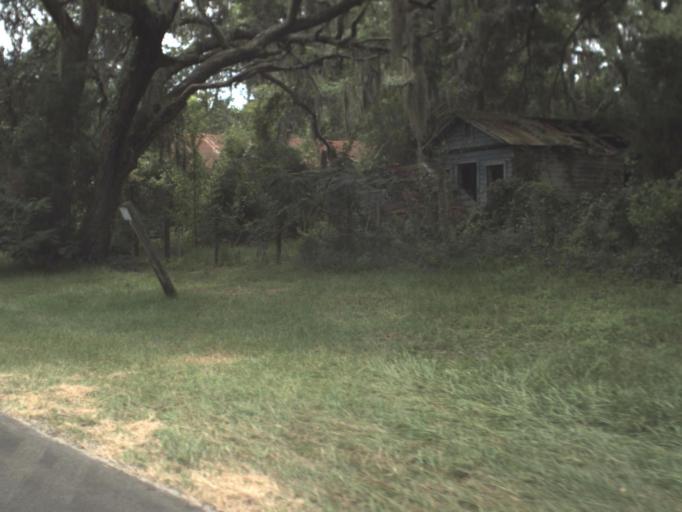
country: US
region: Florida
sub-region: Alachua County
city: Archer
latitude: 29.4938
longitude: -82.4946
